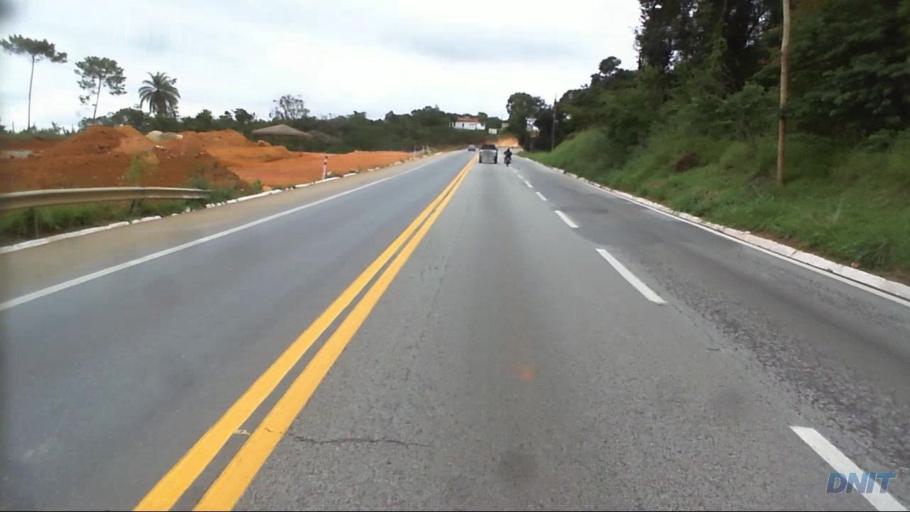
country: BR
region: Minas Gerais
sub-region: Caete
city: Caete
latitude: -19.7452
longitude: -43.5212
